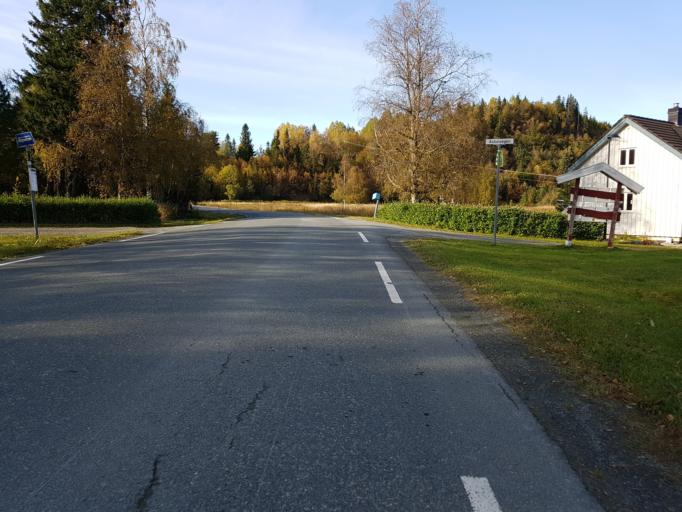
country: NO
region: Sor-Trondelag
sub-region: Klaebu
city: Klaebu
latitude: 63.3465
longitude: 10.5141
